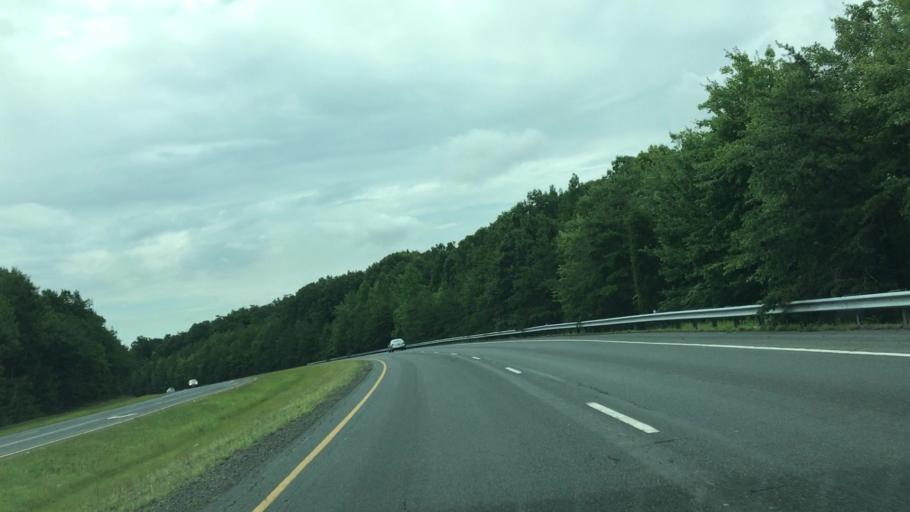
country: US
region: Virginia
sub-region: Prince William County
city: Buckhall
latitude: 38.6893
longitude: -77.3882
